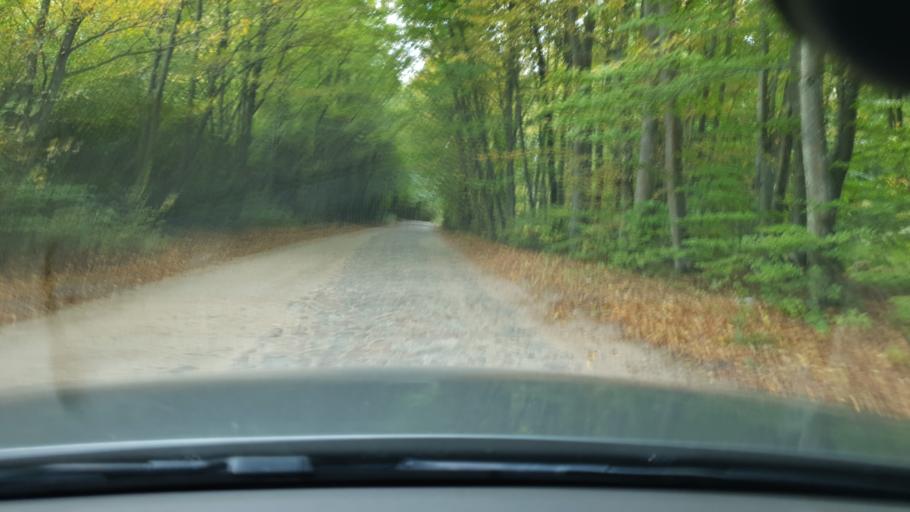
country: PL
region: Pomeranian Voivodeship
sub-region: Powiat wejherowski
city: Reda
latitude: 54.5891
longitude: 18.3307
